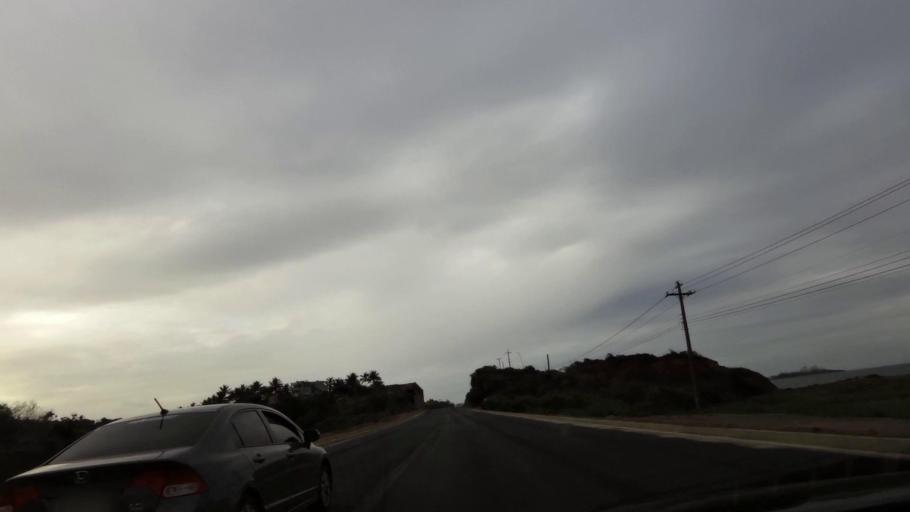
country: BR
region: Espirito Santo
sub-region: Guarapari
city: Guarapari
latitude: -20.7534
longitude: -40.5626
